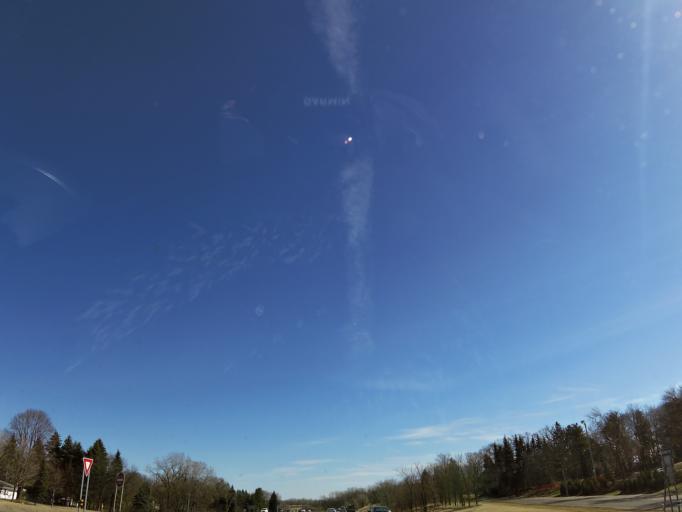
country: US
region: Minnesota
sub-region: Hennepin County
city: Plymouth
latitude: 44.9946
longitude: -93.4368
